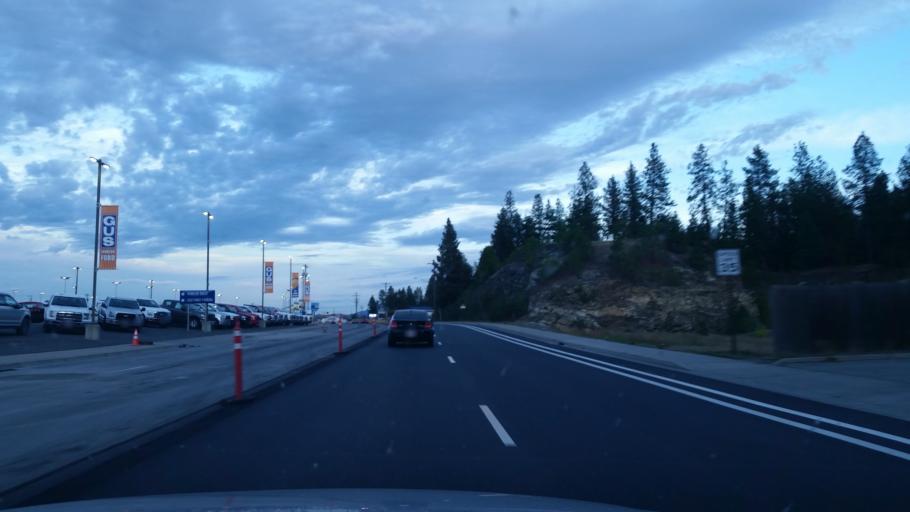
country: US
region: Washington
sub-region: Spokane County
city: Dishman
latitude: 47.6550
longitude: -117.2941
